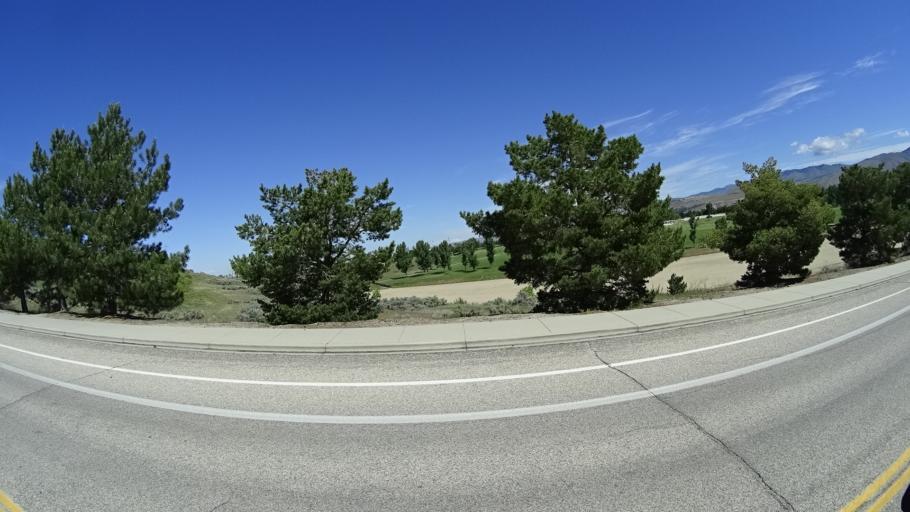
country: US
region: Idaho
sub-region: Ada County
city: Boise
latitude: 43.5435
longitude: -116.1489
